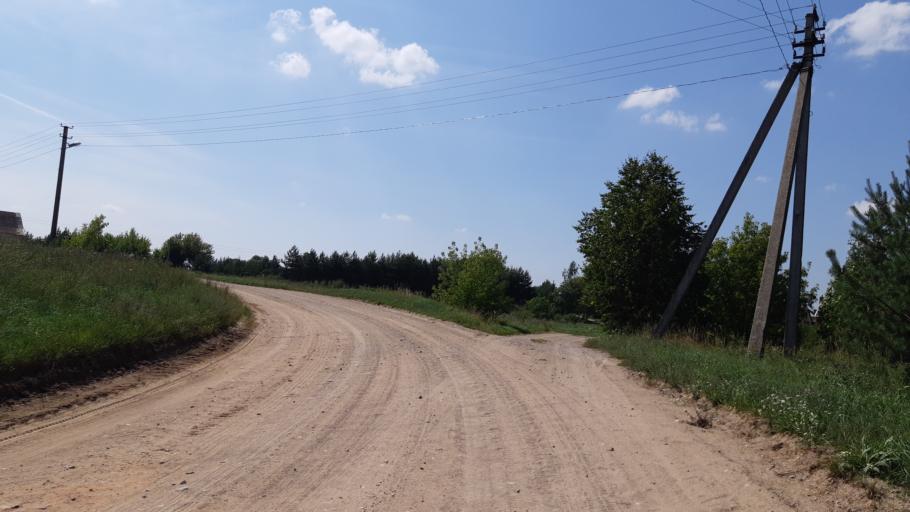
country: LT
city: Virbalis
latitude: 54.6246
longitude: 22.8114
